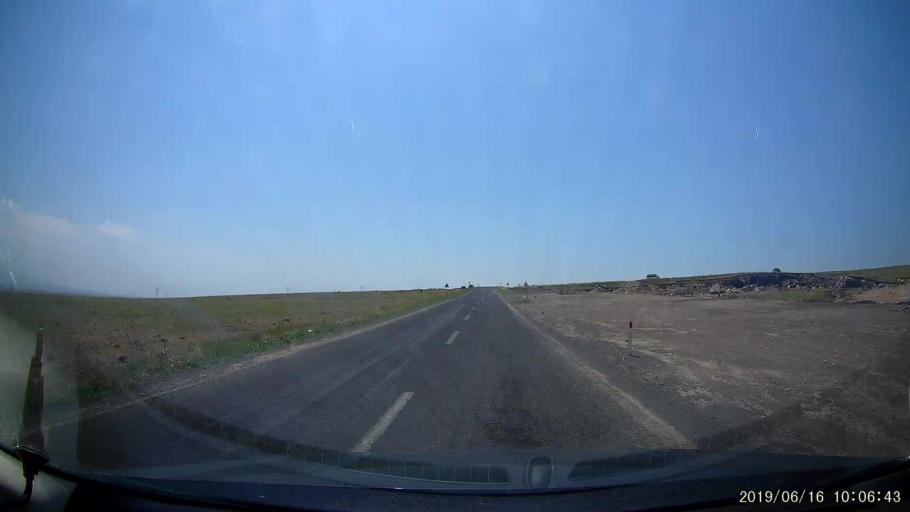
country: TR
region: Kars
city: Digor
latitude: 40.2519
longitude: 43.5457
